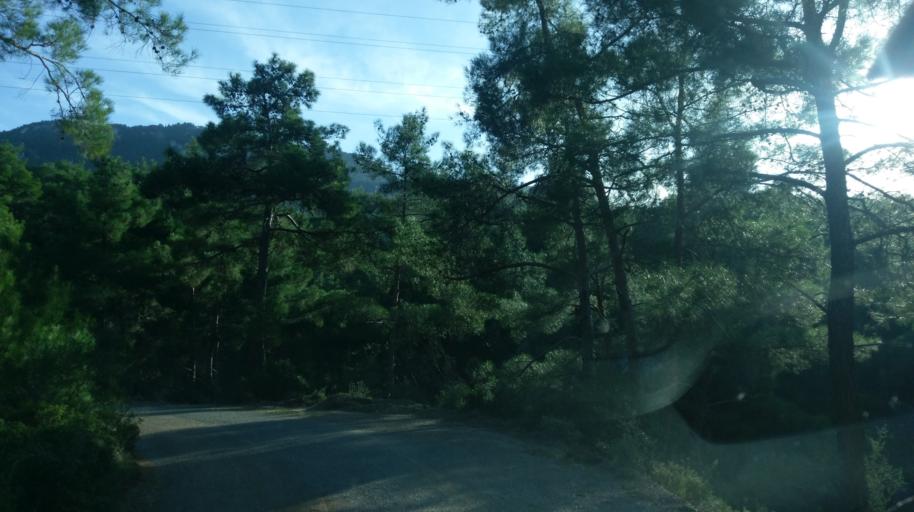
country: CY
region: Ammochostos
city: Lefkonoiko
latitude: 35.3290
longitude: 33.6006
